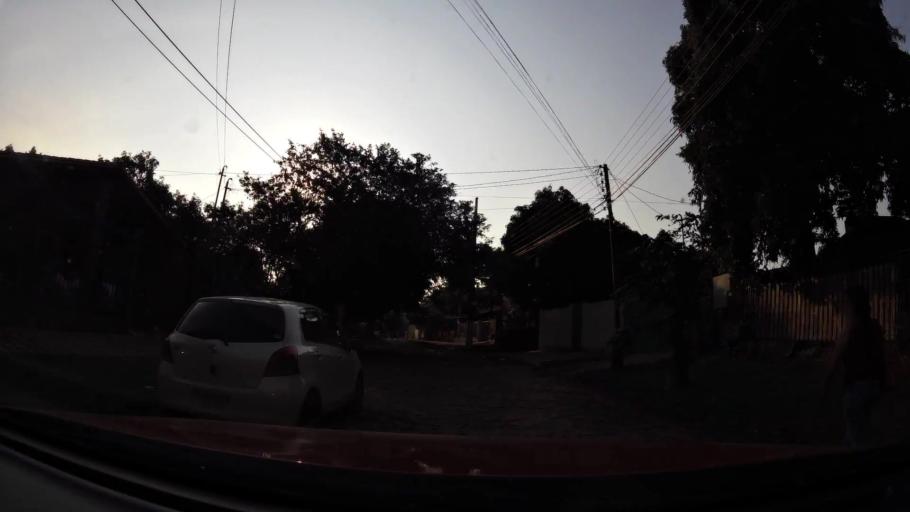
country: PY
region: Central
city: Villa Elisa
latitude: -25.3580
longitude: -57.5995
